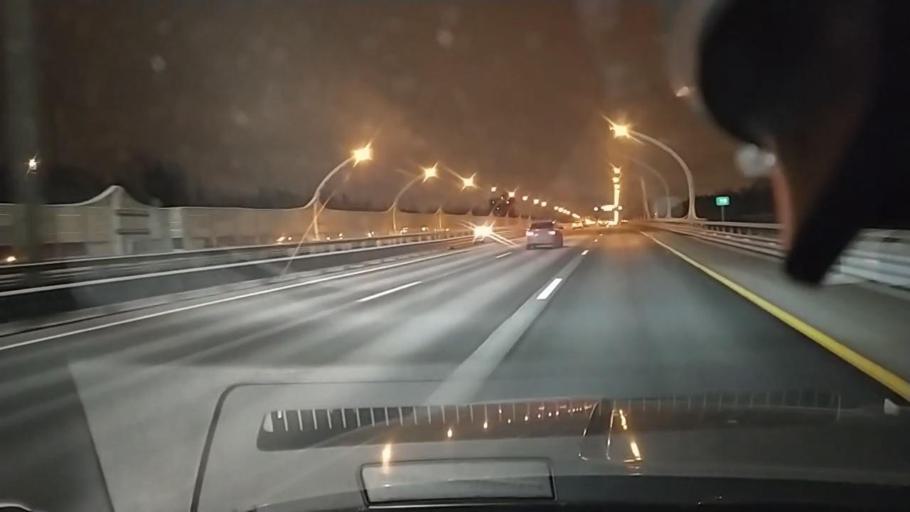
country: RU
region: Leningrad
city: Untolovo
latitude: 60.0291
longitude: 30.2001
